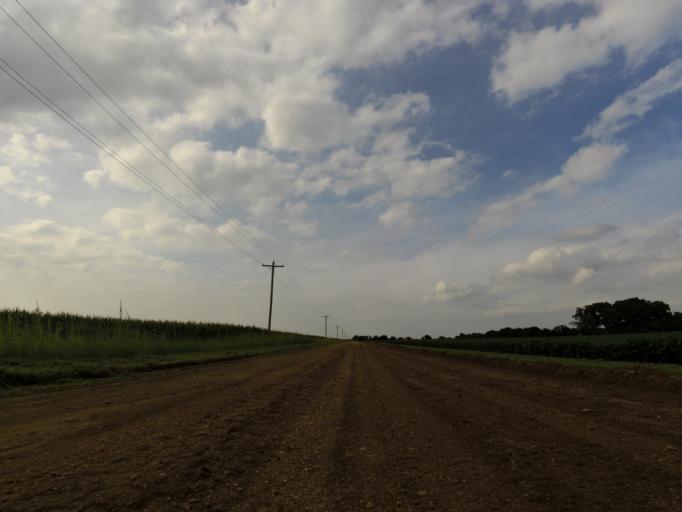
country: US
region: Kansas
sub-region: Reno County
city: South Hutchinson
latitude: 37.8983
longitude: -98.0689
